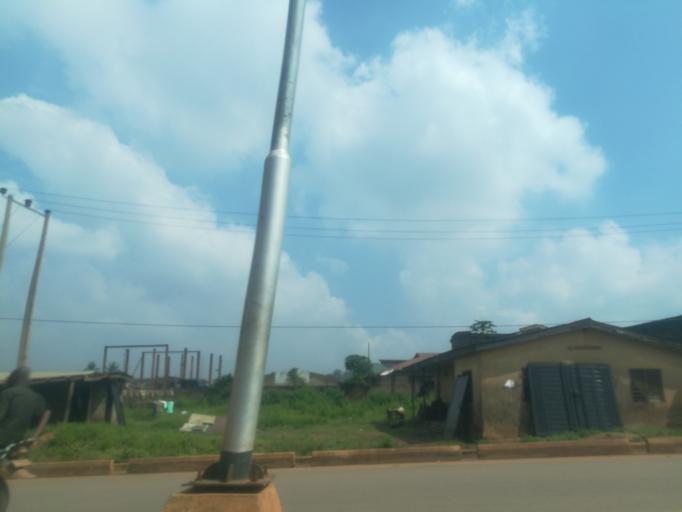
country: NG
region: Oyo
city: Ibadan
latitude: 7.3902
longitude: 3.9398
